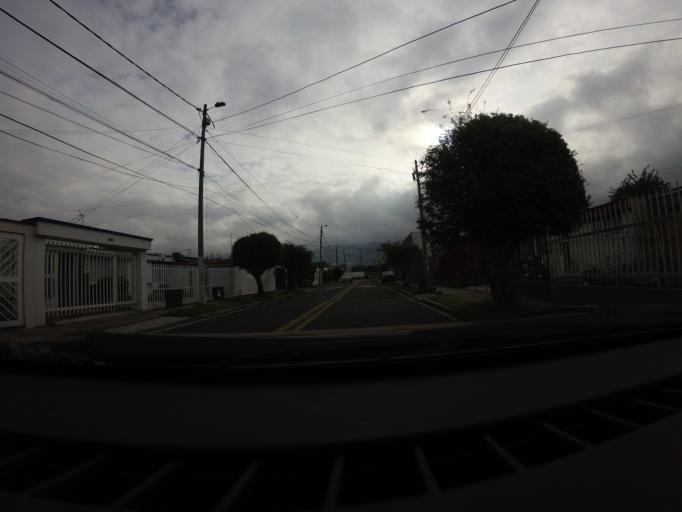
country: CO
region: Bogota D.C.
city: Barrio San Luis
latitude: 4.7097
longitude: -74.0548
